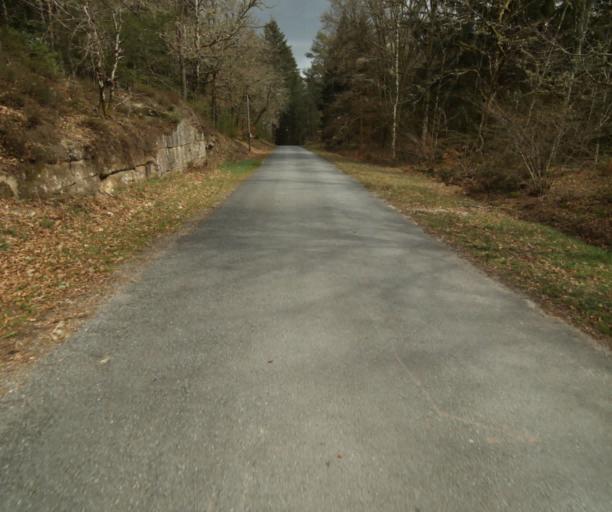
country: FR
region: Limousin
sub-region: Departement de la Correze
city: Correze
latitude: 45.2907
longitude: 1.9533
